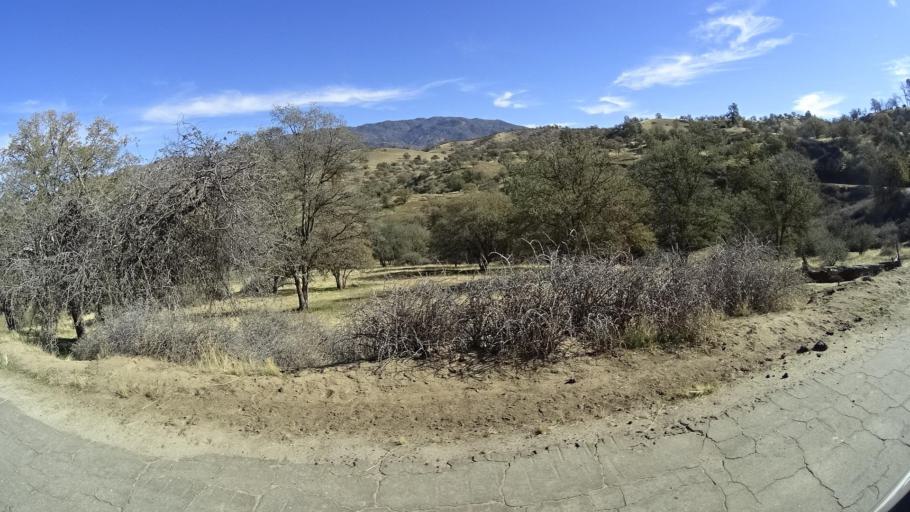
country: US
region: California
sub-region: Kern County
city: Arvin
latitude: 35.4394
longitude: -118.7063
